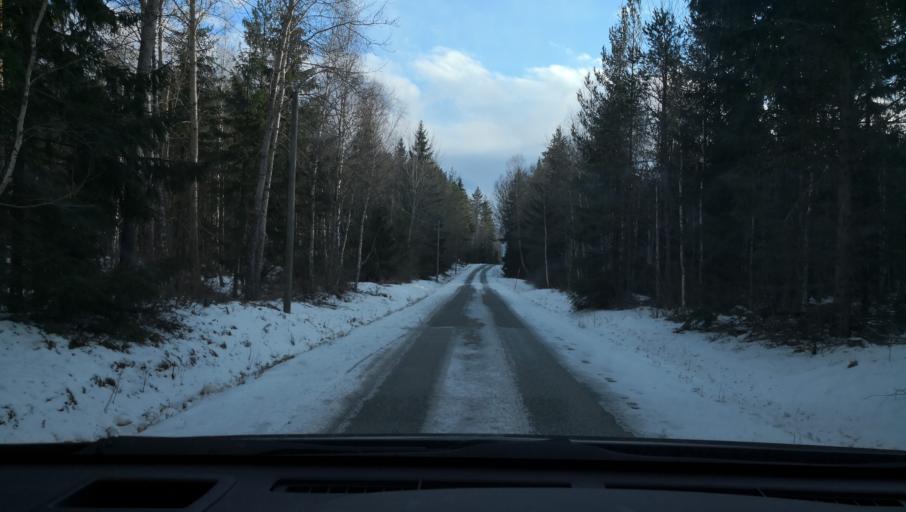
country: SE
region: Uppsala
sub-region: Enkopings Kommun
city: Irsta
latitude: 59.7014
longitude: 16.8685
